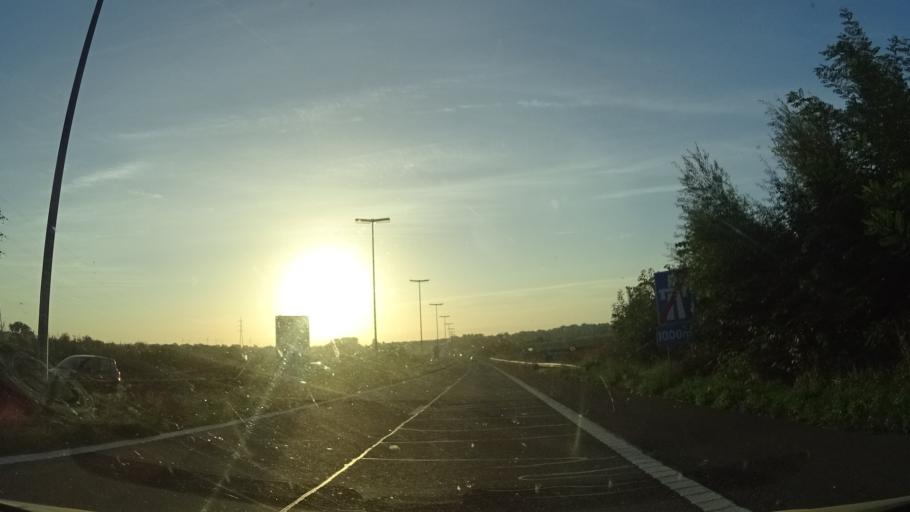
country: BE
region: Wallonia
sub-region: Province du Hainaut
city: Chasse Royale
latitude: 50.4082
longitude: 3.9456
